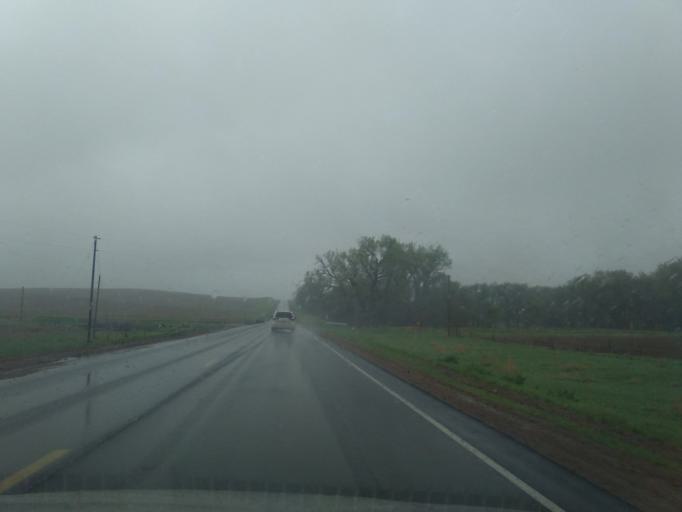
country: US
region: Nebraska
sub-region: Wayne County
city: Wayne
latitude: 42.2224
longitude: -97.1738
